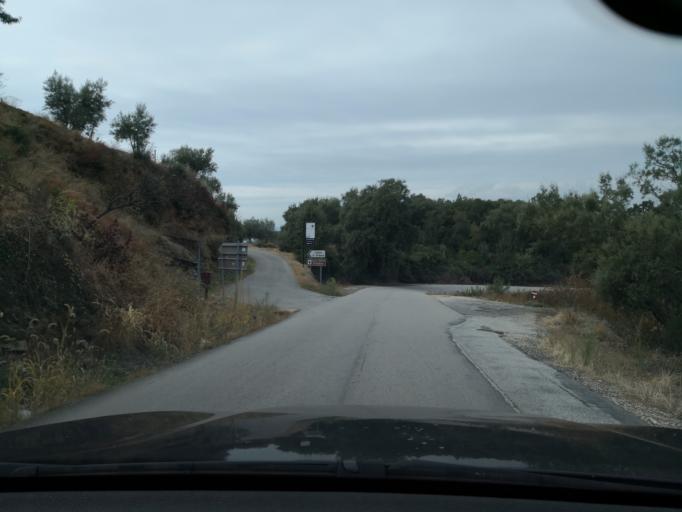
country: PT
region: Vila Real
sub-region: Peso da Regua
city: Peso da Regua
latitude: 41.1974
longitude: -7.7276
